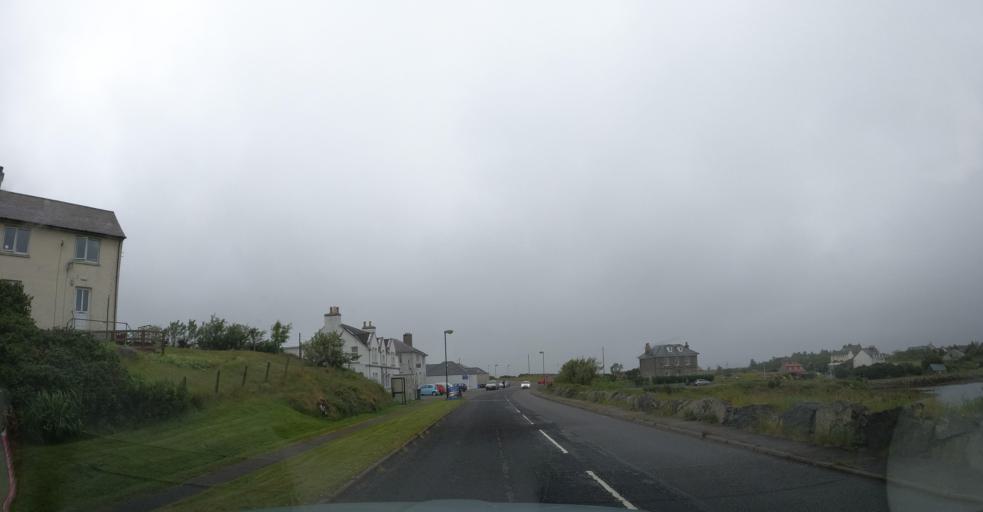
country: GB
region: Scotland
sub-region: Eilean Siar
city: Isle of North Uist
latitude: 57.6012
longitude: -7.1627
